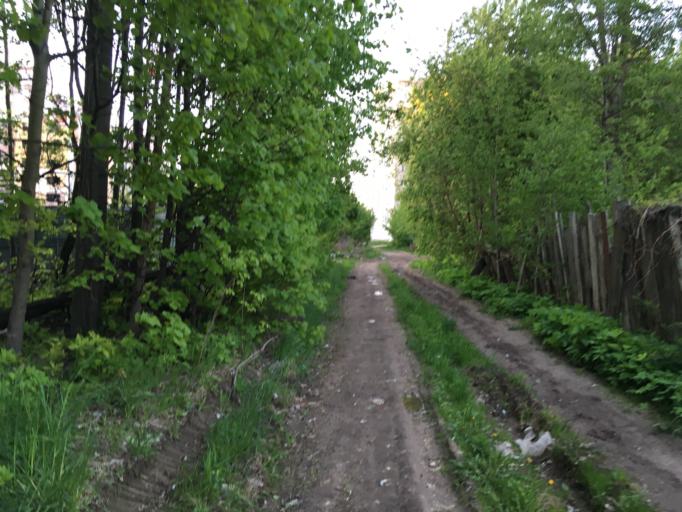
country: RU
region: Mariy-El
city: Yoshkar-Ola
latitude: 56.6322
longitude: 47.9357
